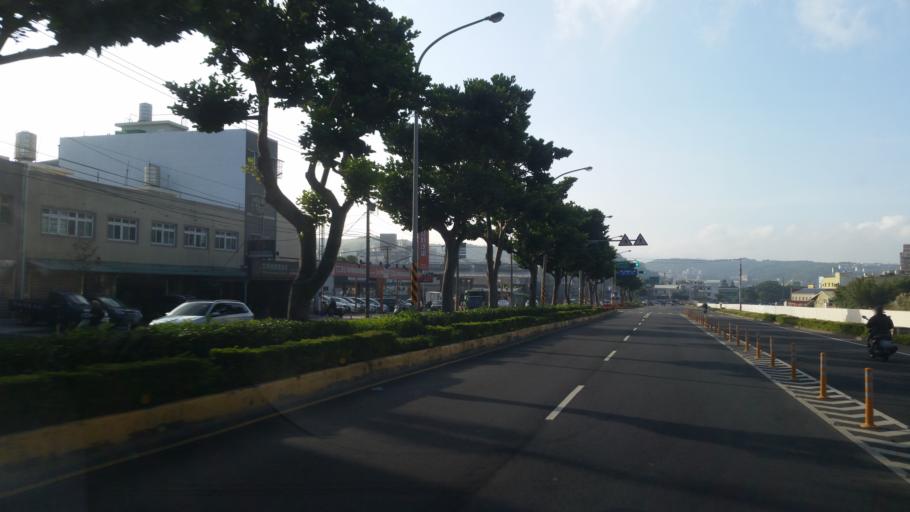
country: TW
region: Taiwan
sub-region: Taoyuan
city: Taoyuan
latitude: 25.0046
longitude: 121.3442
